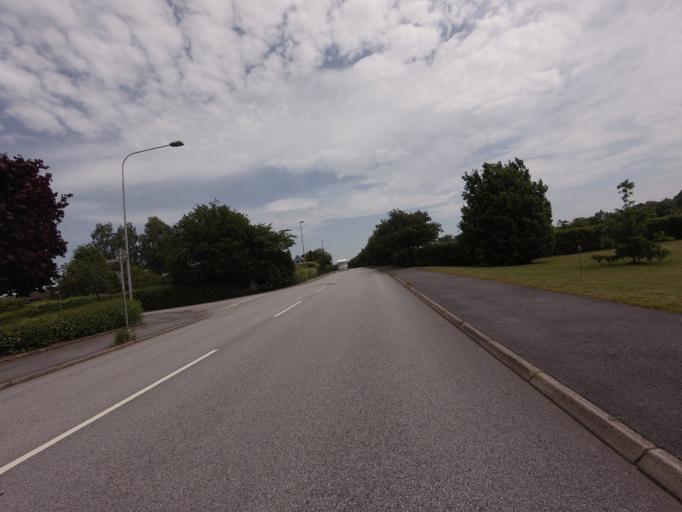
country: SE
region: Skane
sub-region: Ystads Kommun
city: Ystad
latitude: 55.4272
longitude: 13.7917
